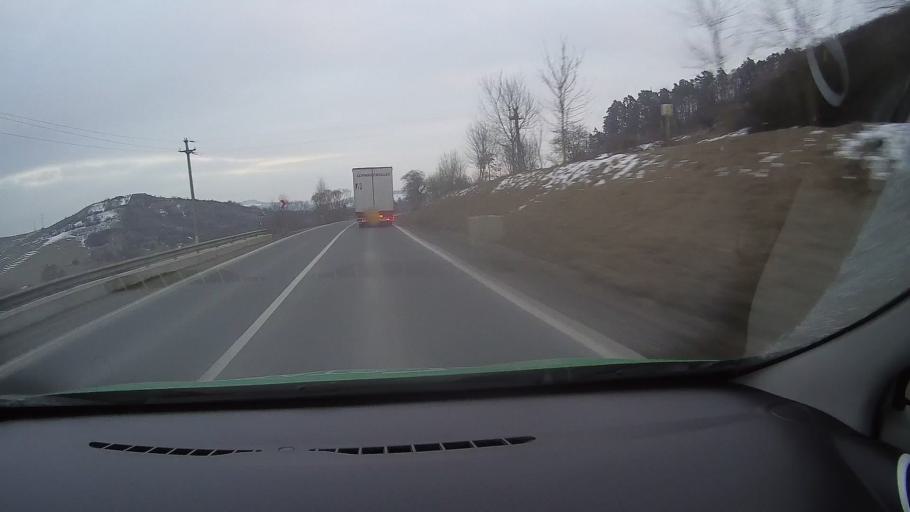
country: RO
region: Harghita
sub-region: Municipiul Odorheiu Secuiesc
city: Odorheiu Secuiesc
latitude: 46.3270
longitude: 25.2778
